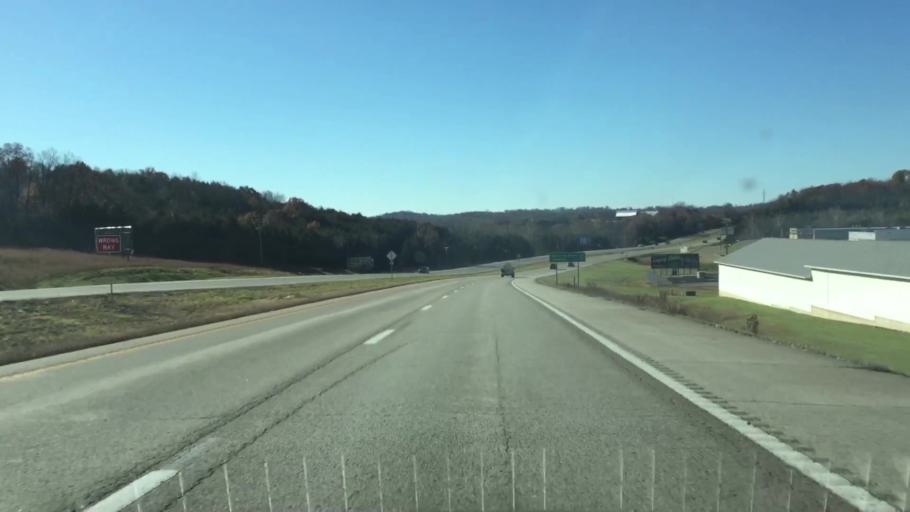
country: US
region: Missouri
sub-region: Cole County
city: Wardsville
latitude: 38.5310
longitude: -92.2199
